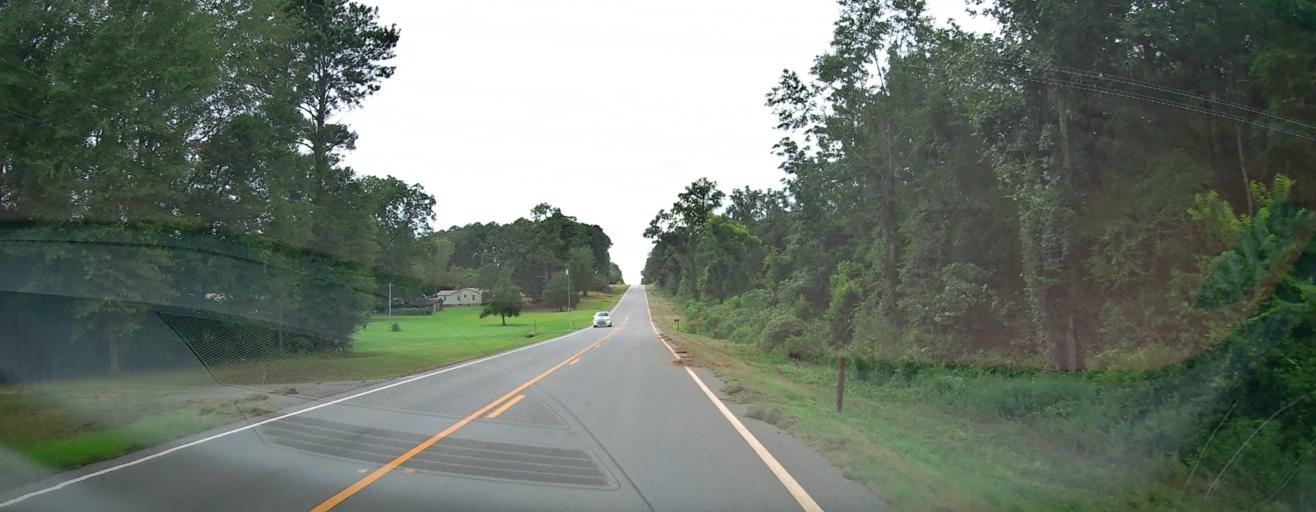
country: US
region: Georgia
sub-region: Macon County
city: Oglethorpe
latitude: 32.2758
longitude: -84.1297
